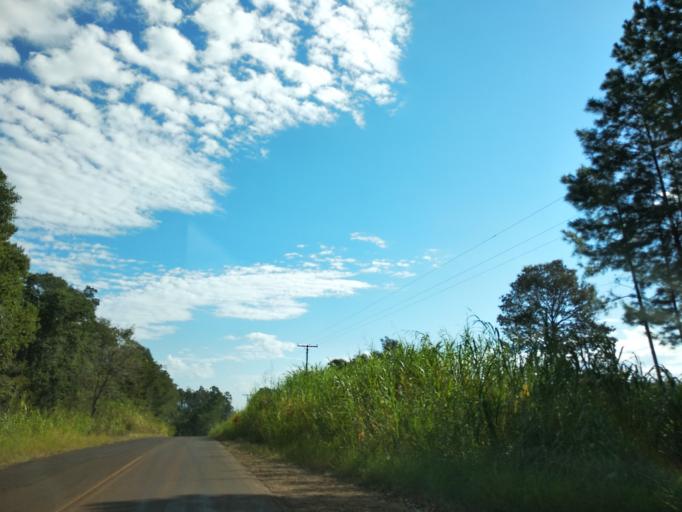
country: AR
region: Misiones
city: Aristobulo del Valle
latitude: -27.0701
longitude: -54.8260
